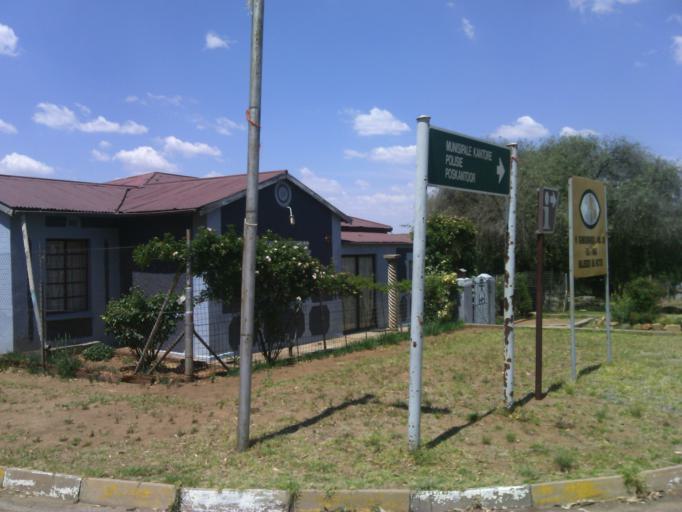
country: ZA
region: Orange Free State
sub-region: Xhariep District Municipality
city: Dewetsdorp
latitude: -29.5821
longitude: 26.6594
